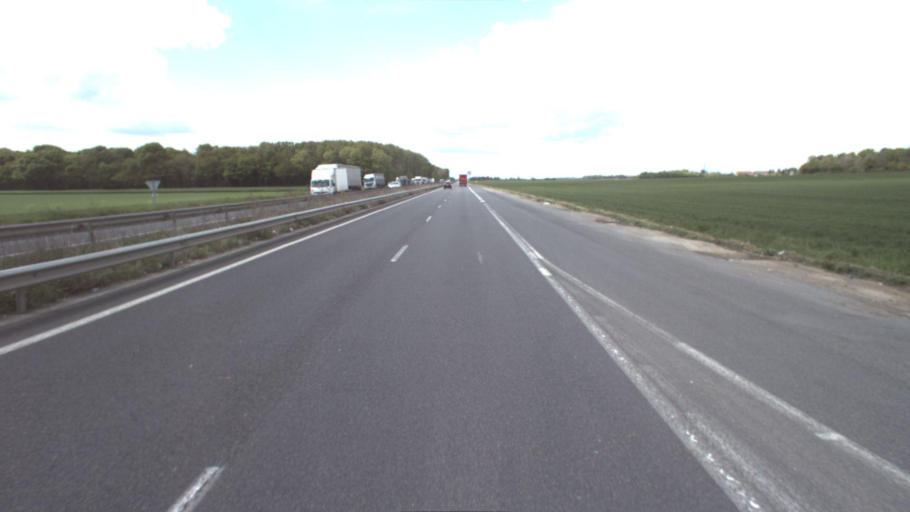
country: FR
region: Ile-de-France
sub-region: Departement de Seine-et-Marne
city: Rozay-en-Brie
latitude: 48.6915
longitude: 2.9173
